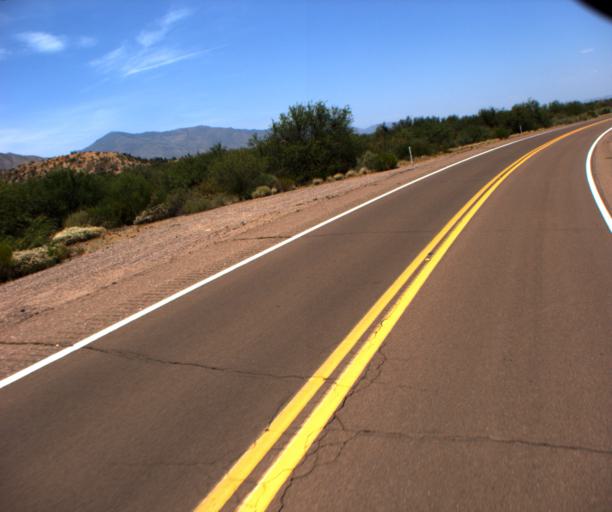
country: US
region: Arizona
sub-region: Gila County
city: Tonto Basin
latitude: 33.8118
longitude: -111.2890
